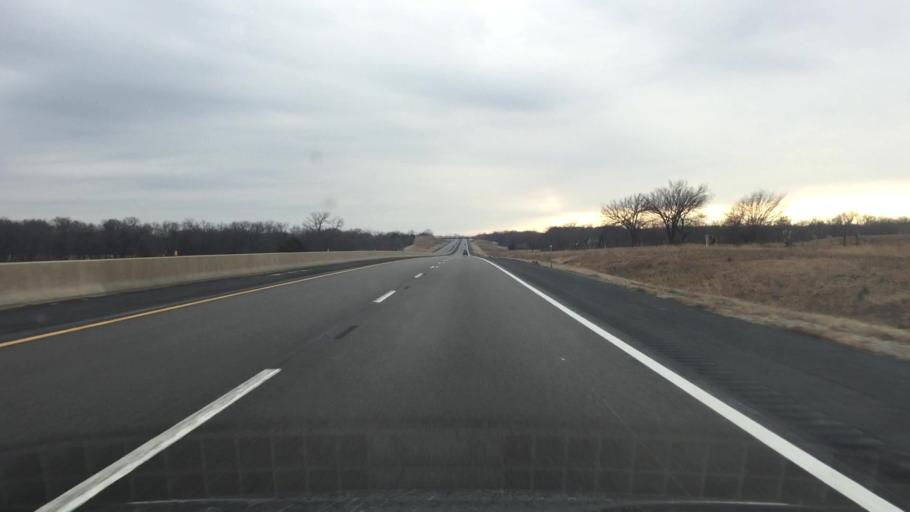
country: US
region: Kansas
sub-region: Osage County
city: Osage City
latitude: 38.7354
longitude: -95.9561
